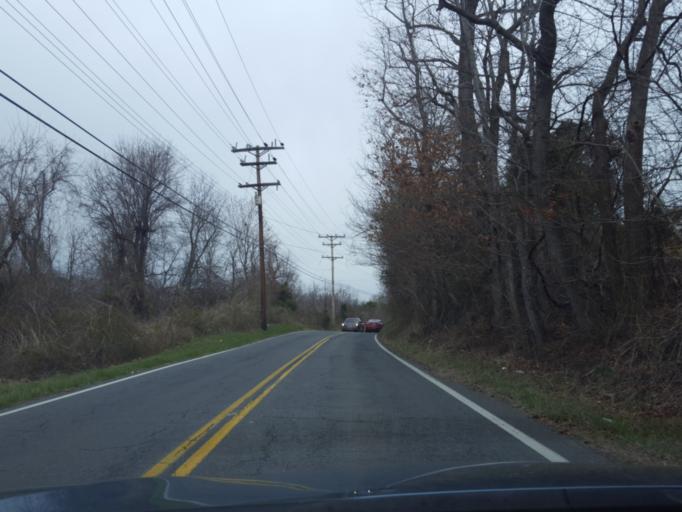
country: US
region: Maryland
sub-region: Calvert County
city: Owings
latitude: 38.7066
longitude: -76.5736
